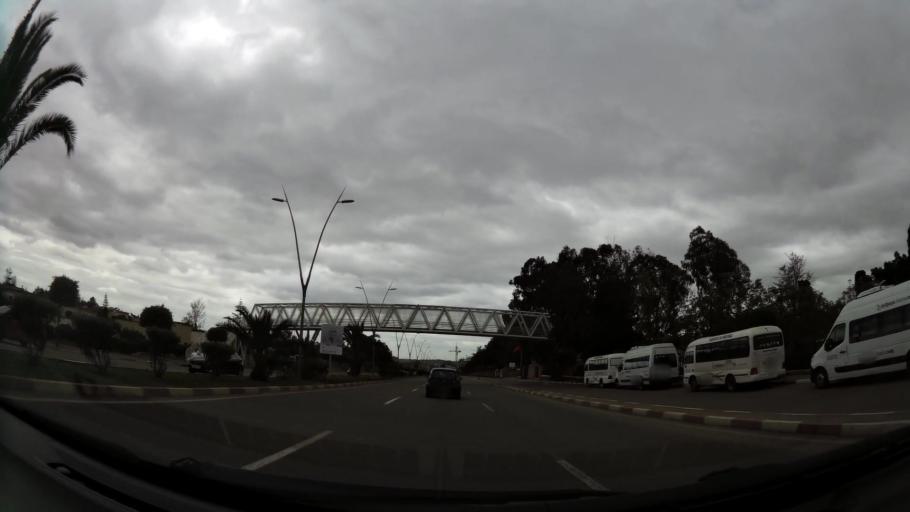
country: MA
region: Grand Casablanca
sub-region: Casablanca
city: Casablanca
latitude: 33.5276
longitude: -7.6364
